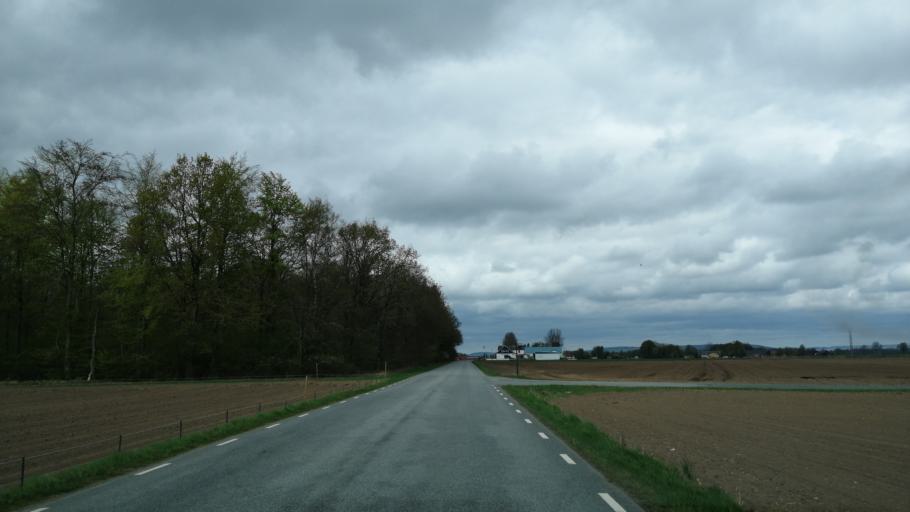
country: SE
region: Skane
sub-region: Kristianstads Kommun
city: Fjalkinge
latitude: 56.0542
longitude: 14.3335
